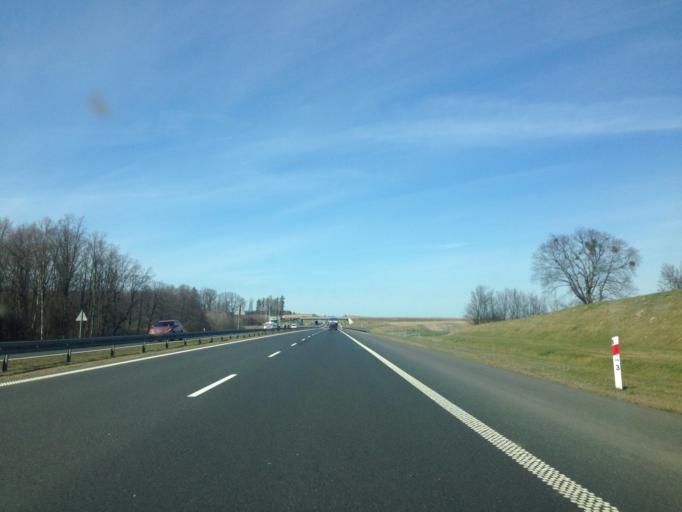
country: PL
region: Pomeranian Voivodeship
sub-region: Powiat starogardzki
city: Bobowo
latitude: 53.8324
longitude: 18.6287
